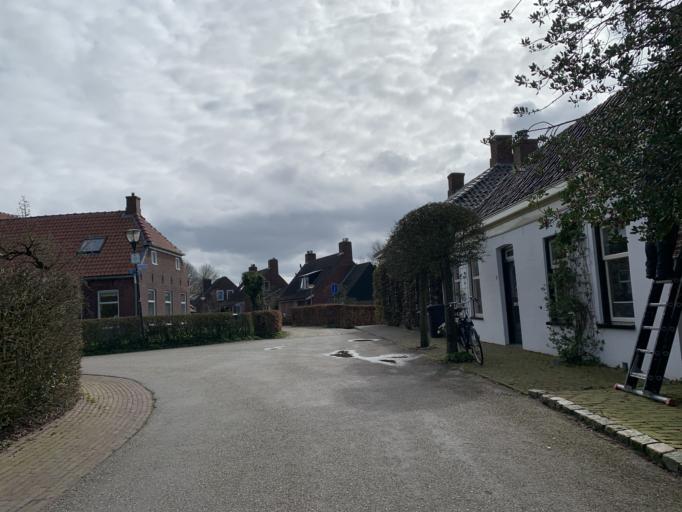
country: NL
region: Groningen
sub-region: Gemeente Groningen
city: Korrewegwijk
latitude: 53.2742
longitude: 6.5315
